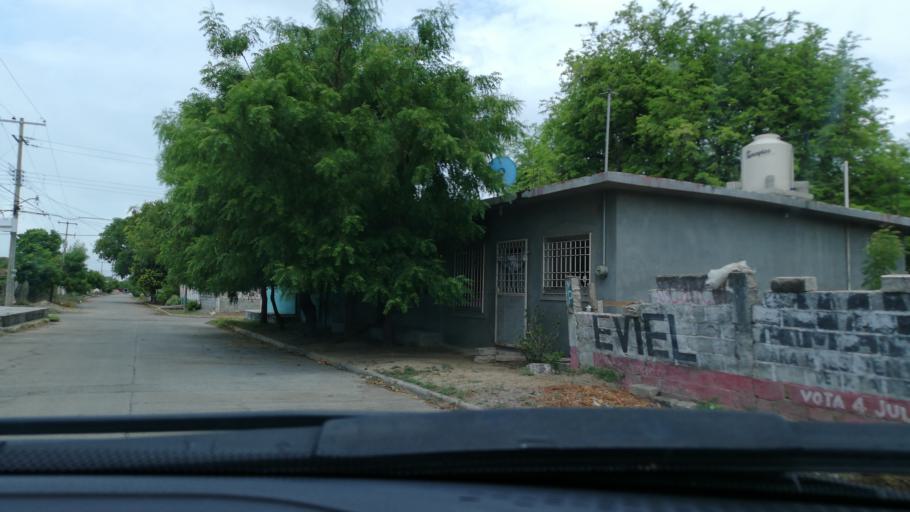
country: MX
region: Oaxaca
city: Asuncion Ixtaltepec
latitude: 16.5087
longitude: -95.0493
